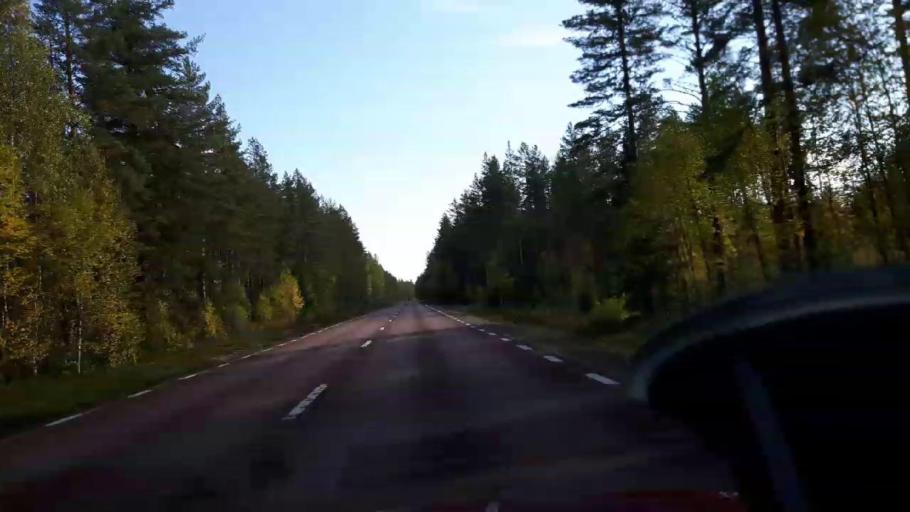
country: SE
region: Gaevleborg
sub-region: Ljusdals Kommun
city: Farila
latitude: 61.9249
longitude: 15.5839
